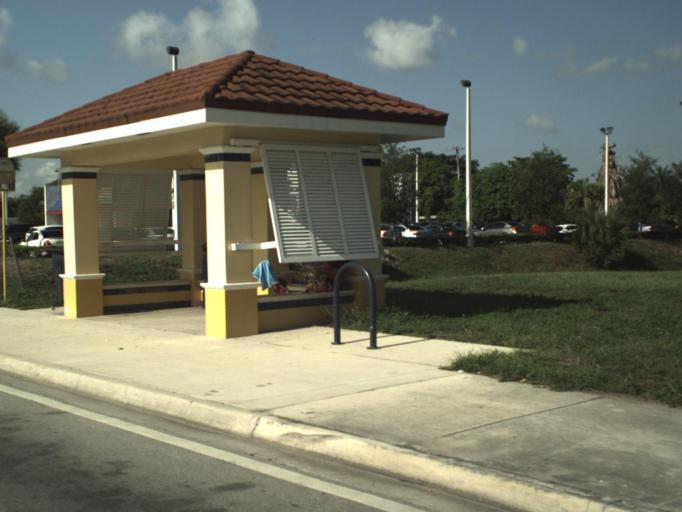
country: US
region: Florida
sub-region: Broward County
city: Margate
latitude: 26.2611
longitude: -80.2018
